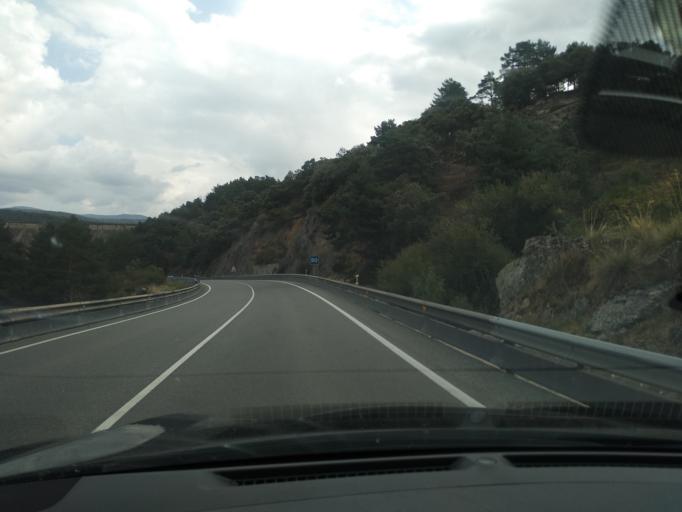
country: ES
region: Castille and Leon
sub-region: Provincia de Segovia
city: Palazuelos de Eresma
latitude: 40.8631
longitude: -4.1010
